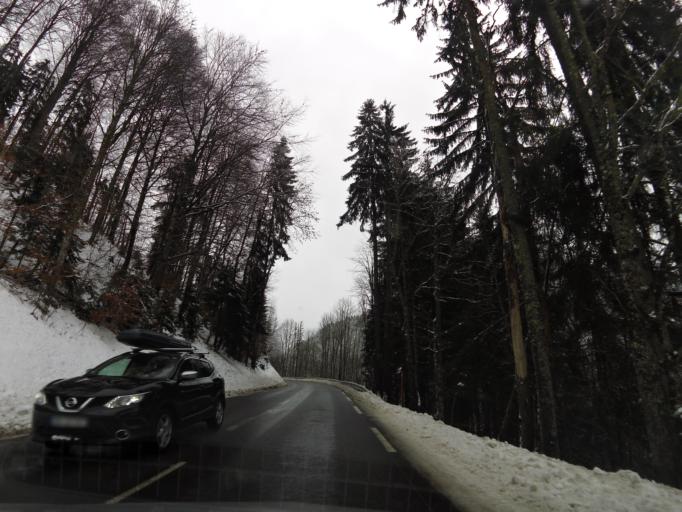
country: FR
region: Rhone-Alpes
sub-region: Departement de la Haute-Savoie
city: Morzine
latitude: 46.1843
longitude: 6.6816
